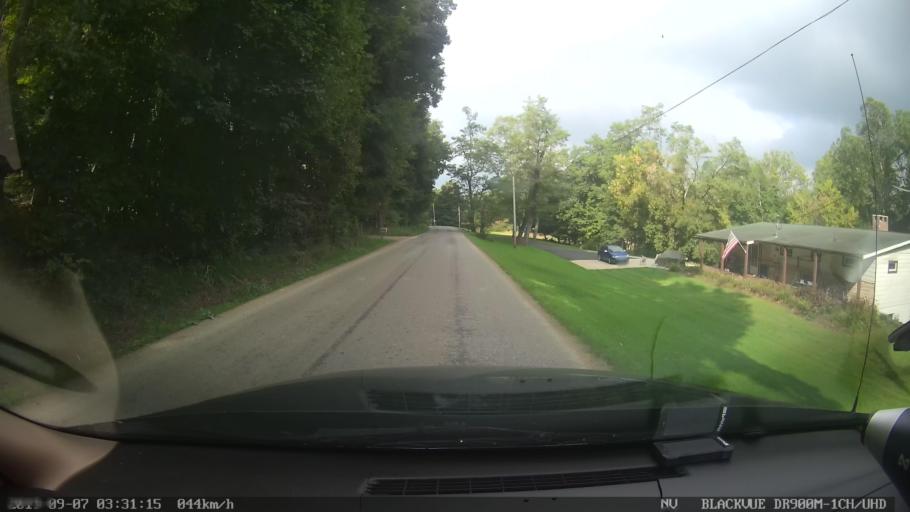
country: US
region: Ohio
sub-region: Licking County
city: Granville
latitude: 40.1193
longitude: -82.5285
